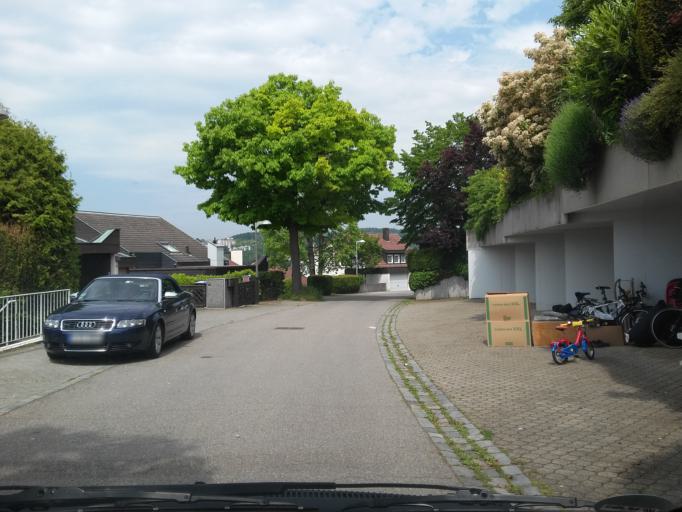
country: DE
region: Baden-Wuerttemberg
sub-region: Regierungsbezirk Stuttgart
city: Esslingen
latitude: 48.7521
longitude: 9.3276
